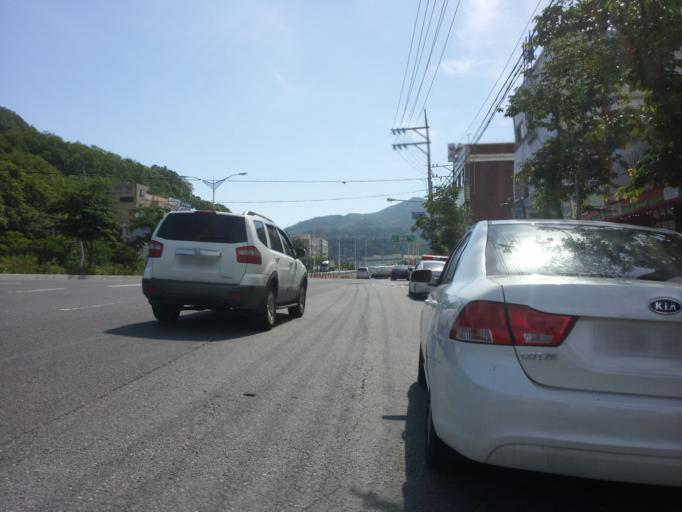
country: KR
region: Daejeon
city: Daejeon
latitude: 36.3184
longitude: 127.4631
